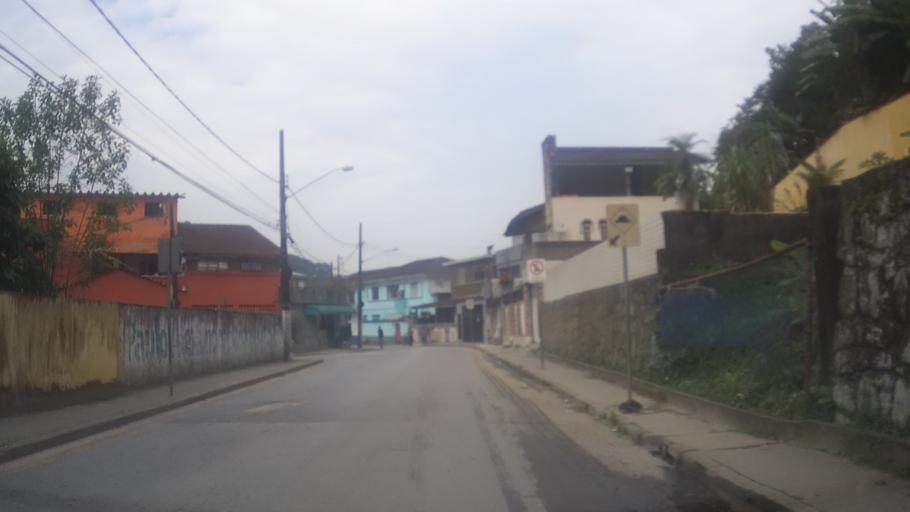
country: BR
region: Sao Paulo
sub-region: Santos
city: Santos
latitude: -23.9427
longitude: -46.3532
